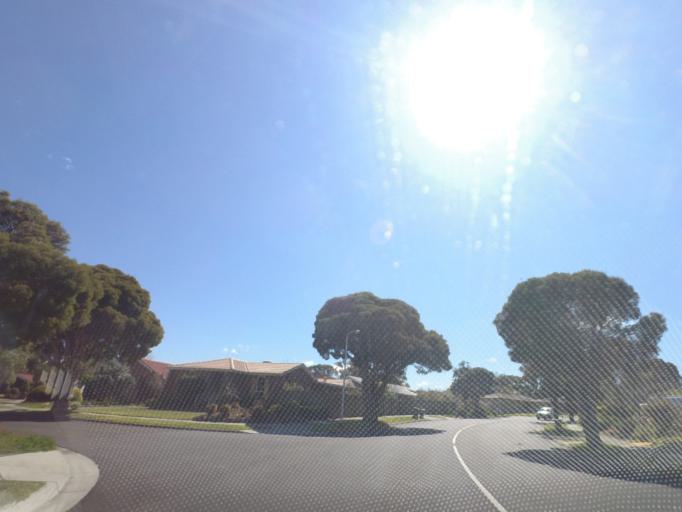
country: AU
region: Victoria
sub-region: Knox
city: Wantirna South
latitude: -37.8950
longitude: 145.2186
